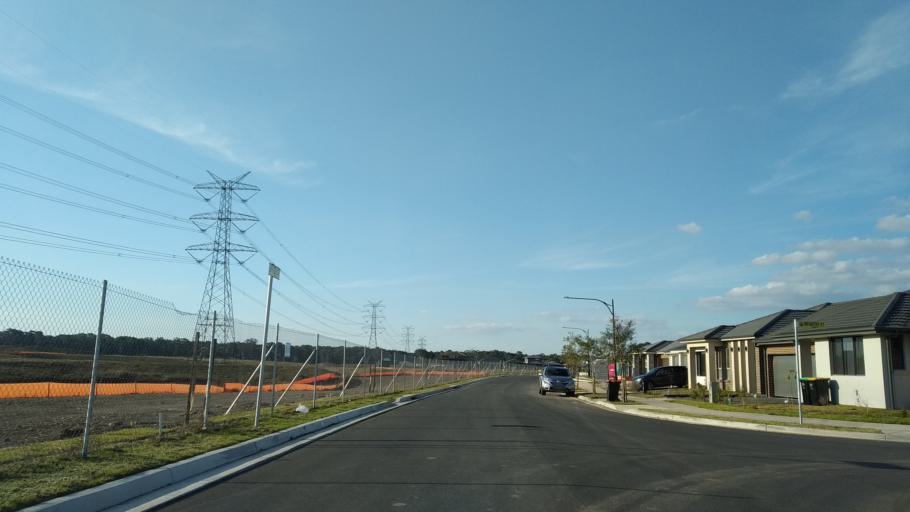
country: AU
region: New South Wales
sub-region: Penrith Municipality
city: Werrington County
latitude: -33.7321
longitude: 150.7533
